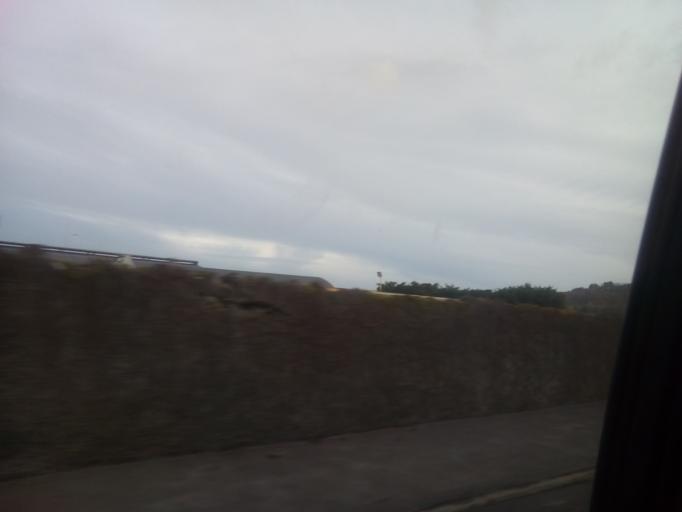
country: IE
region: Leinster
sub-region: Laois
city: Abbeyleix
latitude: 52.8435
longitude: -7.3986
